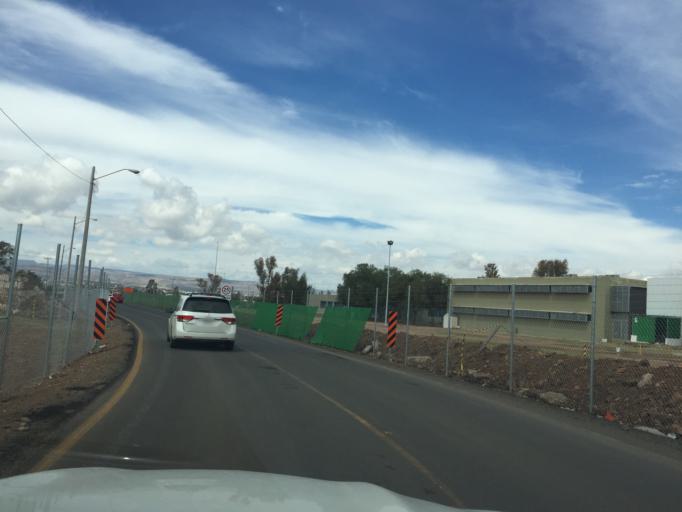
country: MX
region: Aguascalientes
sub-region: Aguascalientes
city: Pocitos
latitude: 21.9097
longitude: -102.3161
